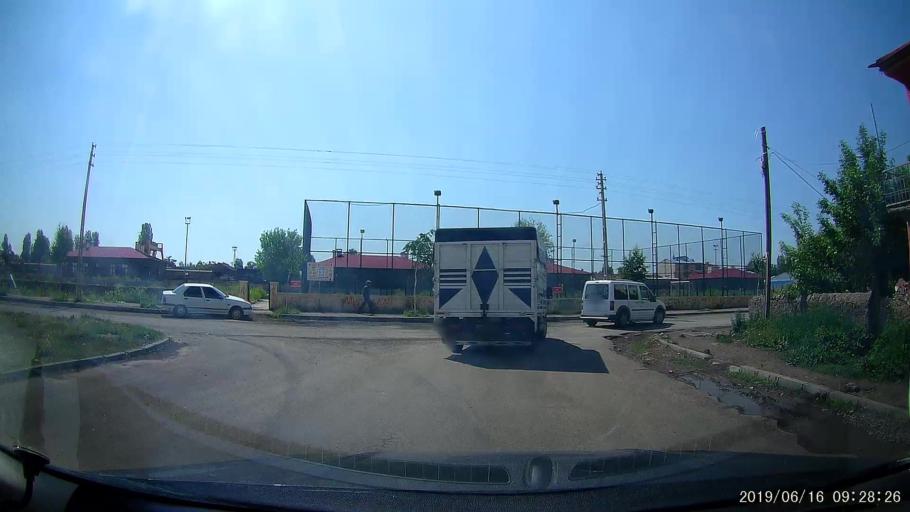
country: TR
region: Kars
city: Kars
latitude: 40.6032
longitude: 43.1038
